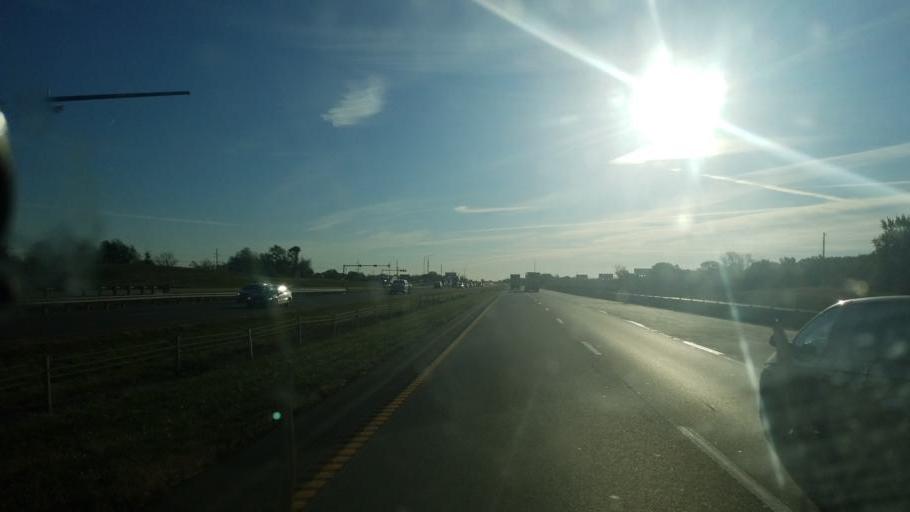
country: US
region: Missouri
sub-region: Saint Charles County
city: Wentzville
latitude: 38.8116
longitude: -90.9347
